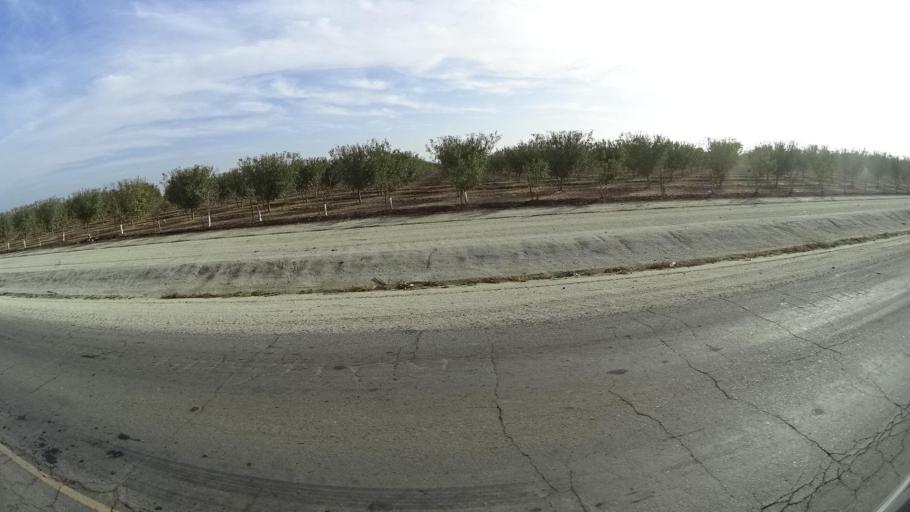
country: US
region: California
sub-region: Kern County
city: McFarland
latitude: 35.6994
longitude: -119.2049
